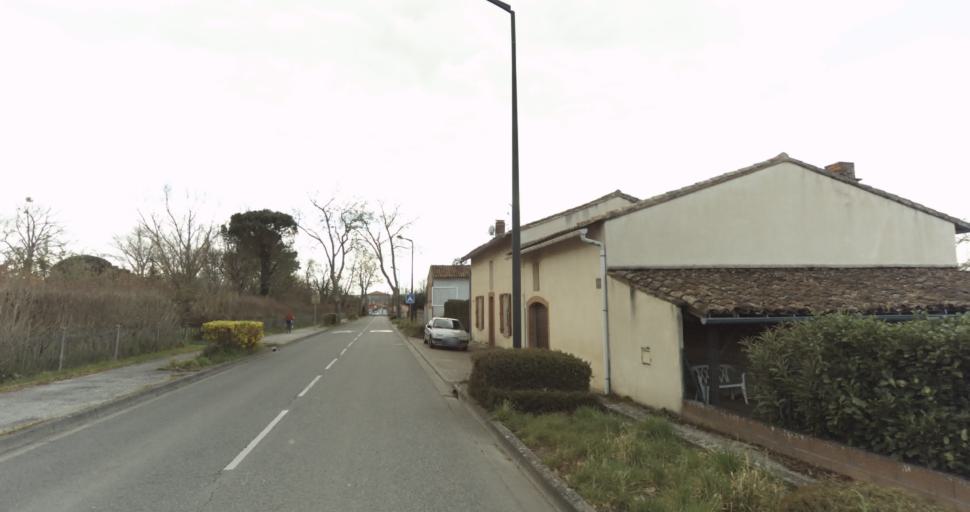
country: FR
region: Midi-Pyrenees
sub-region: Departement de la Haute-Garonne
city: Auterive
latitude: 43.3535
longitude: 1.4844
